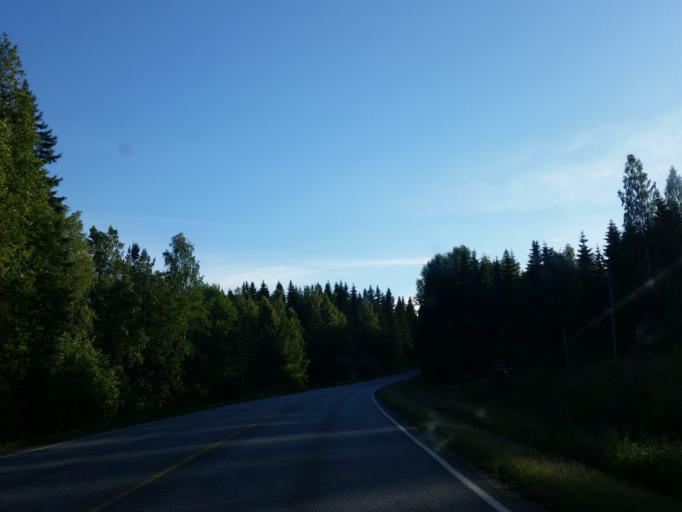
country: FI
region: Northern Savo
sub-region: Kuopio
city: Karttula
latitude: 62.8656
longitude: 27.1420
